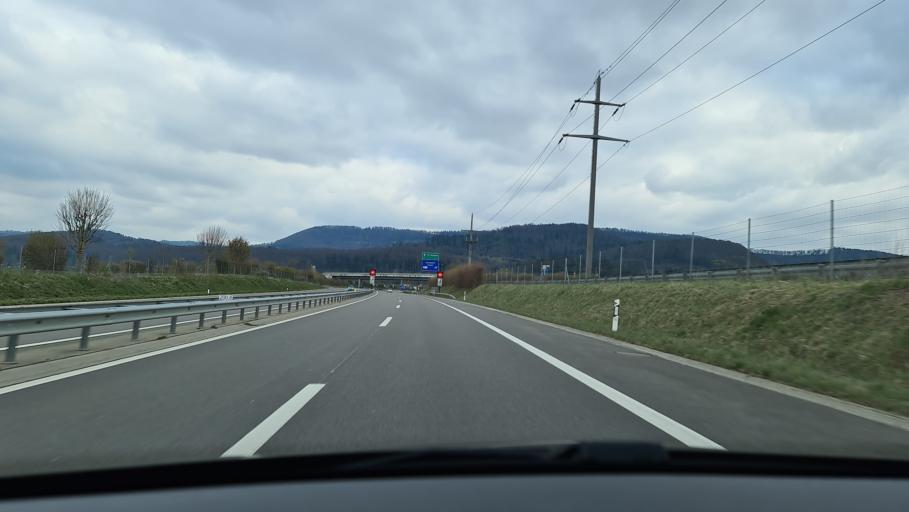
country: CH
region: Jura
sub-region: Porrentruy District
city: Courgenay
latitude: 47.4081
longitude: 7.1396
